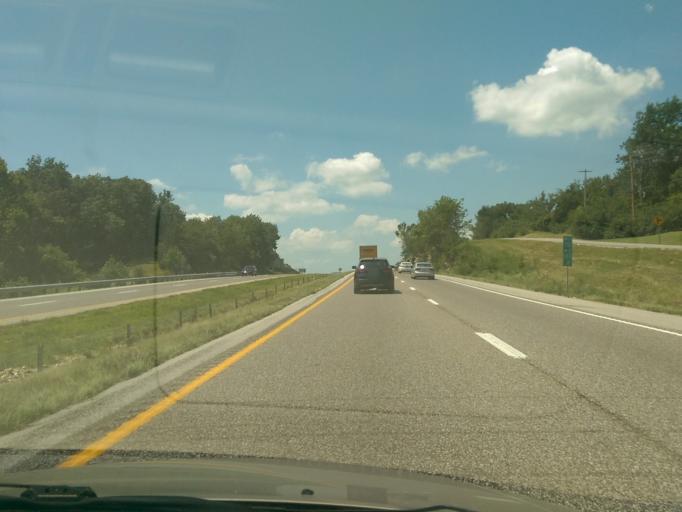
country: US
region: Missouri
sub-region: Boone County
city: Columbia
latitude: 38.9698
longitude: -92.3838
